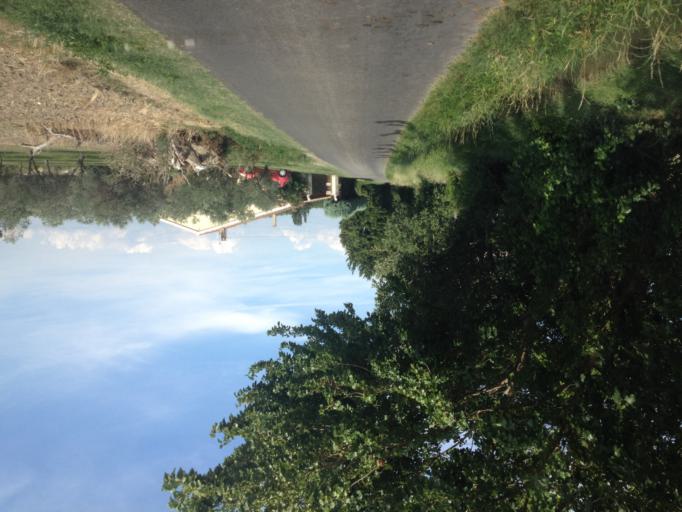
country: FR
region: Provence-Alpes-Cote d'Azur
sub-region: Departement du Vaucluse
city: Orange
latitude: 44.1482
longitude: 4.8327
